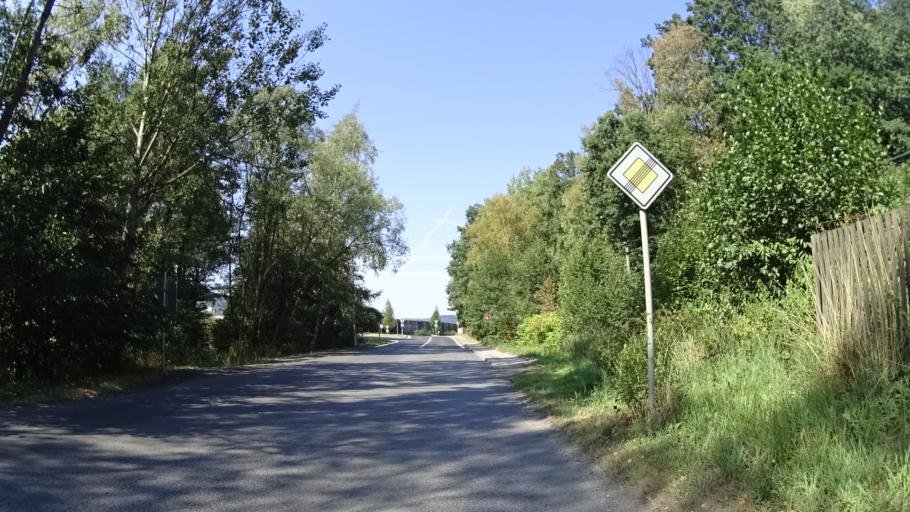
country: CZ
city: Straz nad Nisou
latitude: 50.7909
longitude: 15.0189
